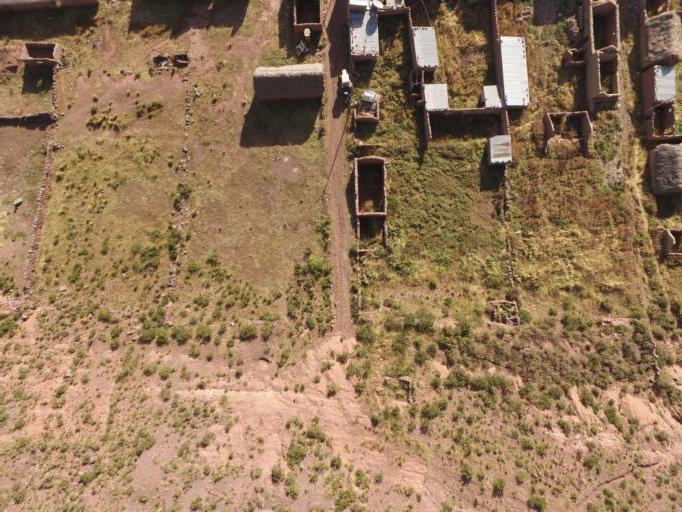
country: BO
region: Oruro
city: Challapata
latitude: -18.6925
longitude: -66.7561
